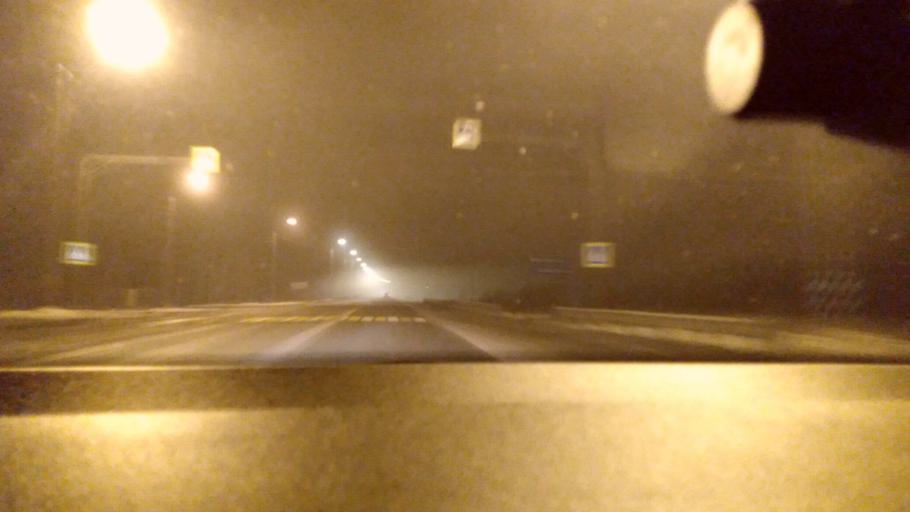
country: RU
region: Moskovskaya
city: Yegor'yevsk
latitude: 55.3927
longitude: 39.0726
